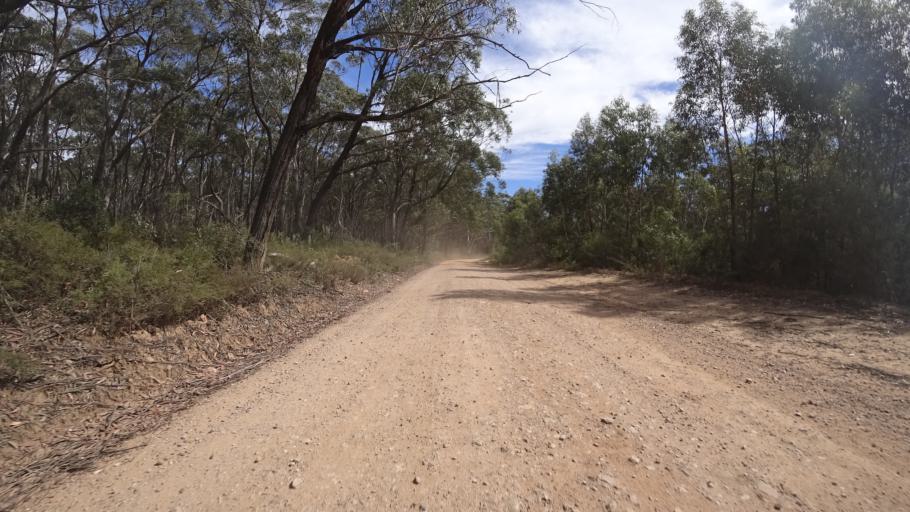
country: AU
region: New South Wales
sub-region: Lithgow
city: Lithgow
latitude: -33.3280
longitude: 150.2485
